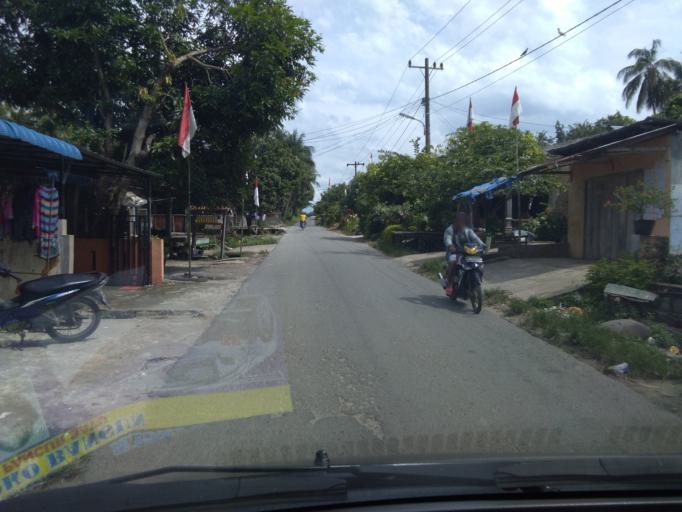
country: ID
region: North Sumatra
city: Deli Tua
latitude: 3.3045
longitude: 98.8082
